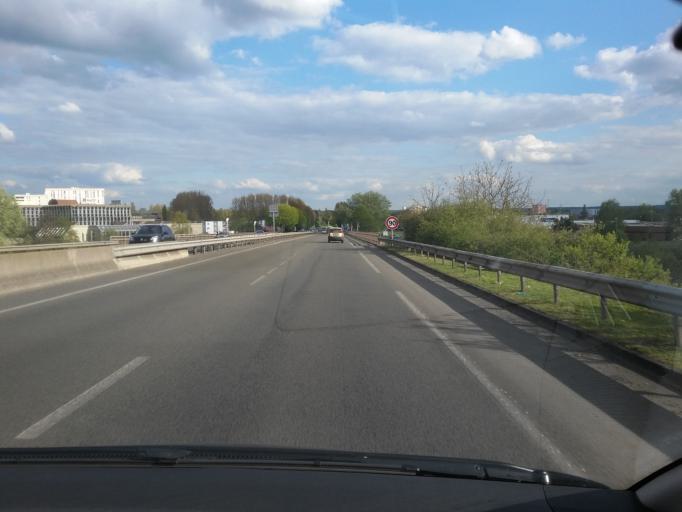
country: FR
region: Picardie
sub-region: Departement de l'Oise
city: Jaux
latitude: 49.3995
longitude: 2.7862
